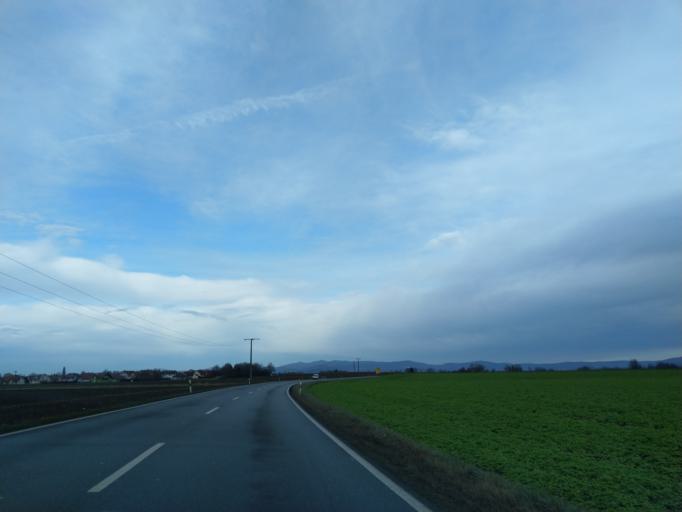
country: DE
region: Bavaria
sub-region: Lower Bavaria
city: Osterhofen
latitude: 48.6808
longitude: 13.0311
